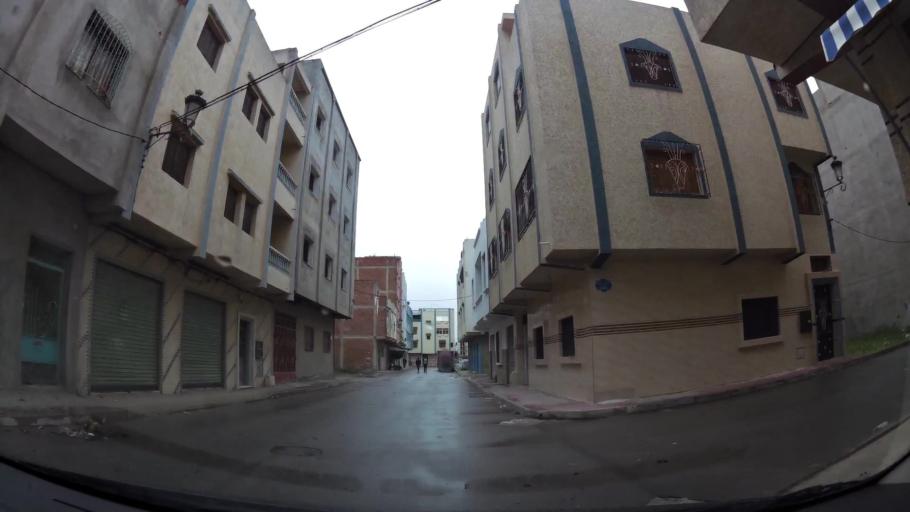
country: MA
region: Tanger-Tetouan
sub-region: Tetouan
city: Martil
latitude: 35.6164
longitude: -5.2861
